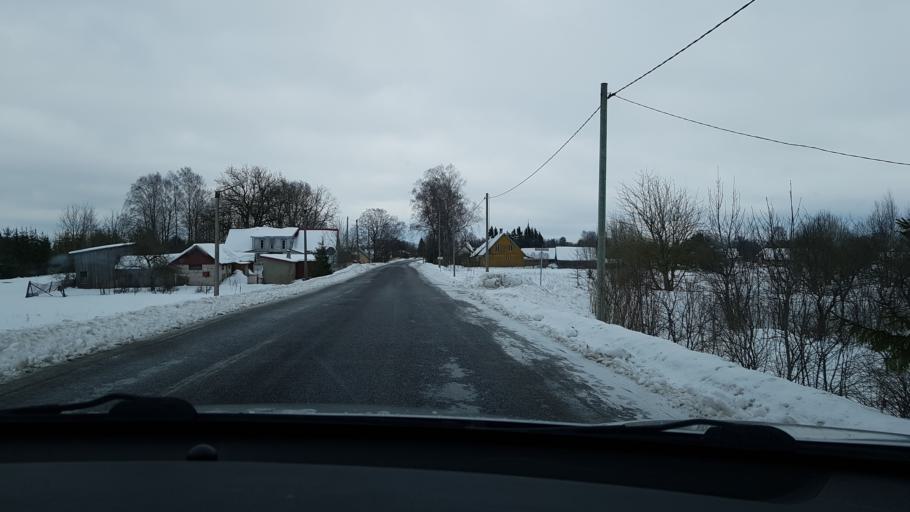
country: EE
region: Jaervamaa
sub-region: Koeru vald
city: Koeru
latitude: 58.9690
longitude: 26.0195
